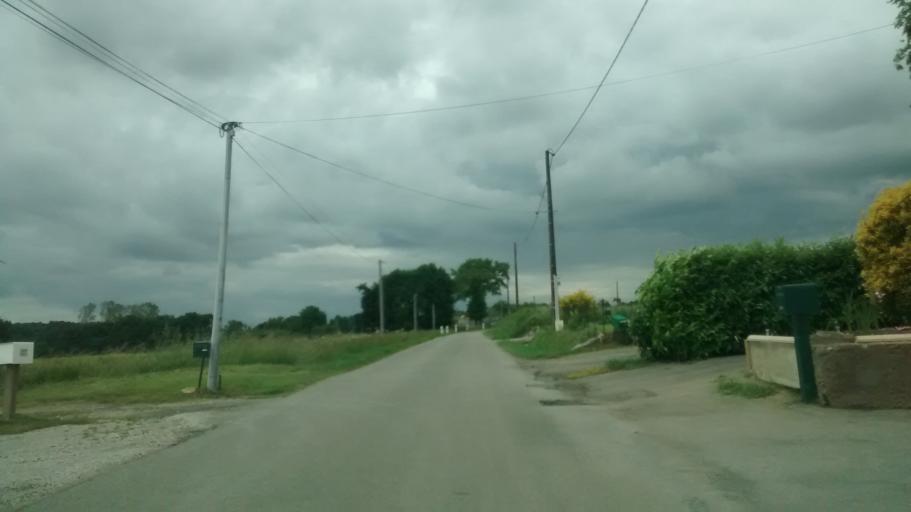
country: FR
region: Brittany
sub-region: Departement du Morbihan
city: Carentoir
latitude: 47.7975
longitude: -2.1078
